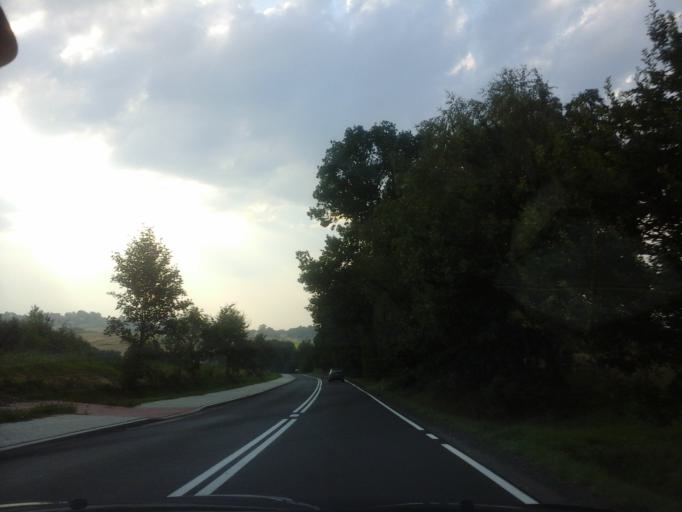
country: PL
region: Lesser Poland Voivodeship
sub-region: Powiat wadowicki
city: Ryczow
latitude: 49.9720
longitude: 19.5649
